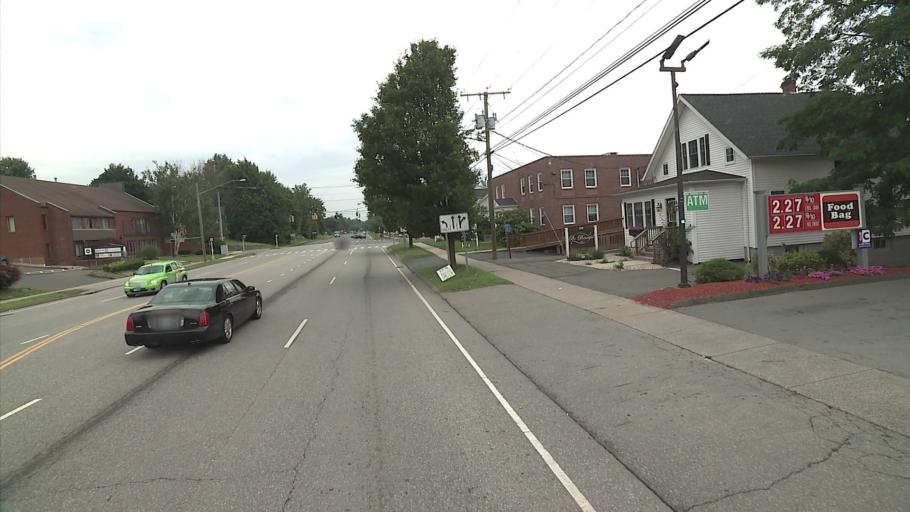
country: US
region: Connecticut
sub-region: Hartford County
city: Wethersfield
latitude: 41.7161
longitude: -72.6650
